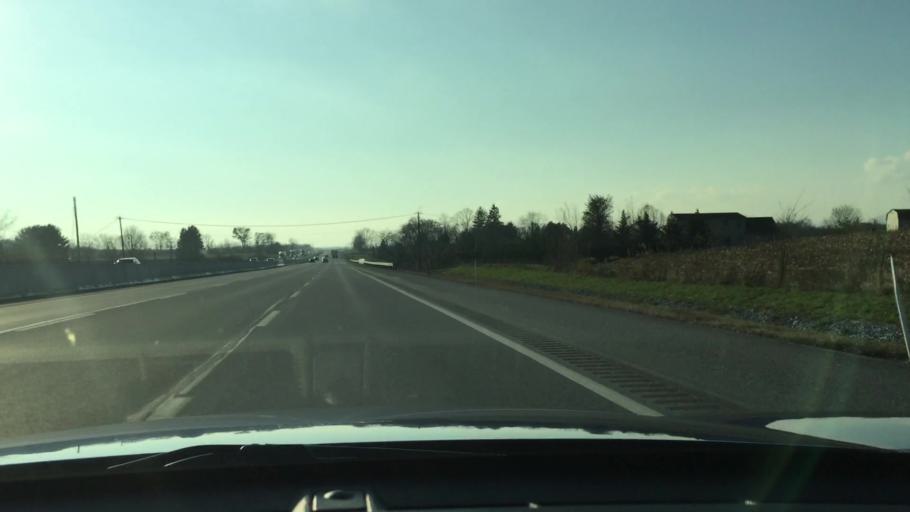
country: US
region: Pennsylvania
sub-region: Cumberland County
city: Carlisle
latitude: 40.2149
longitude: -77.2056
